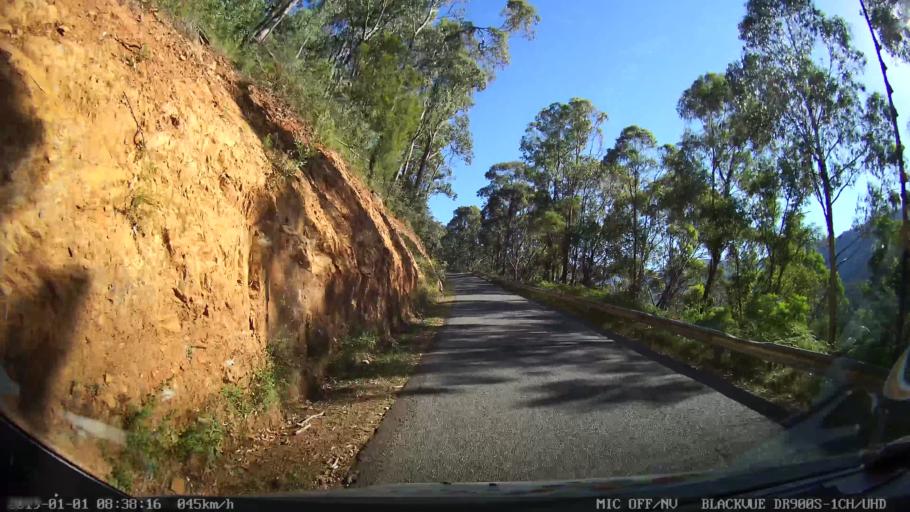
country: AU
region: New South Wales
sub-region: Snowy River
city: Jindabyne
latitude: -36.3333
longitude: 148.1977
